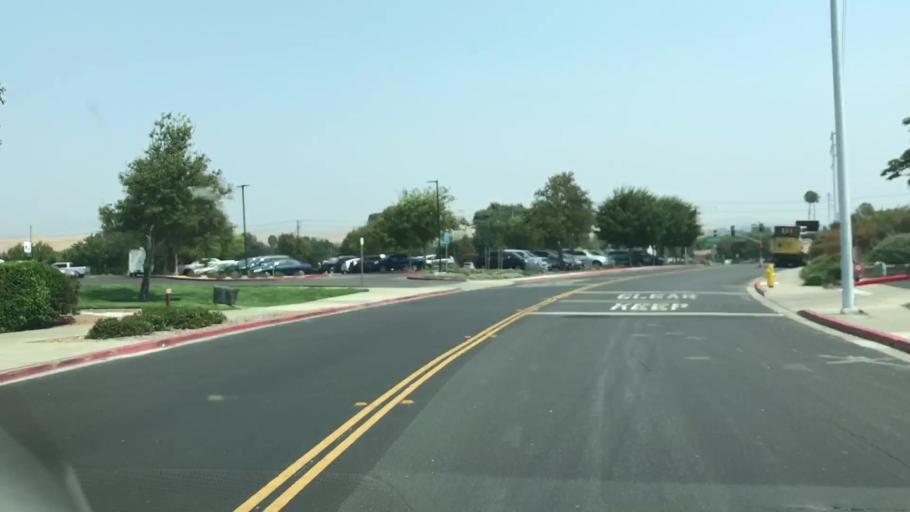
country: US
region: California
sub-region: Alameda County
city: Dublin
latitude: 37.7137
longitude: -121.9415
